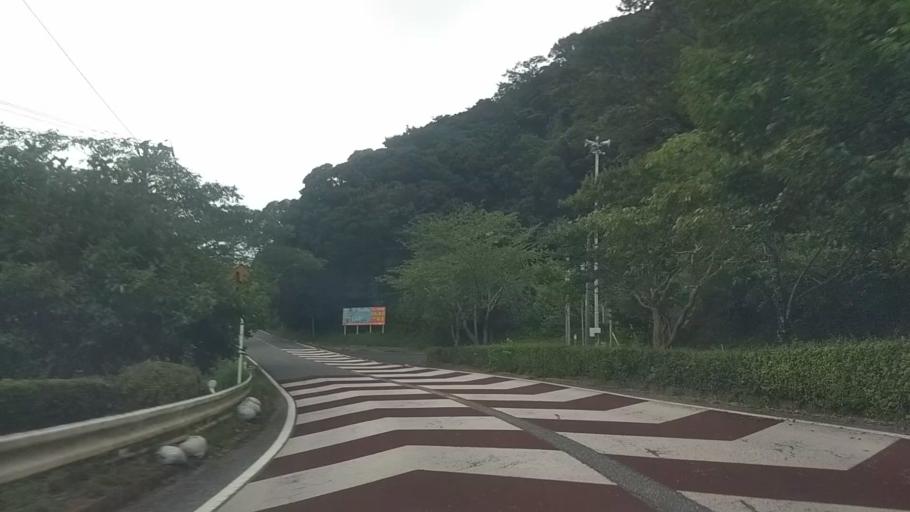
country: JP
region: Chiba
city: Tateyama
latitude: 35.1435
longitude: 139.9158
